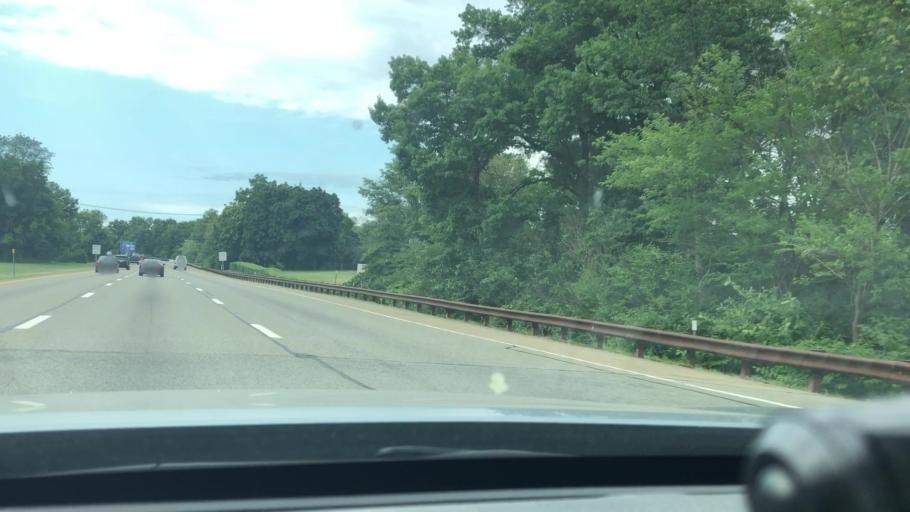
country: US
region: New Jersey
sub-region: Passaic County
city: Clifton
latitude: 40.8501
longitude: -74.1784
